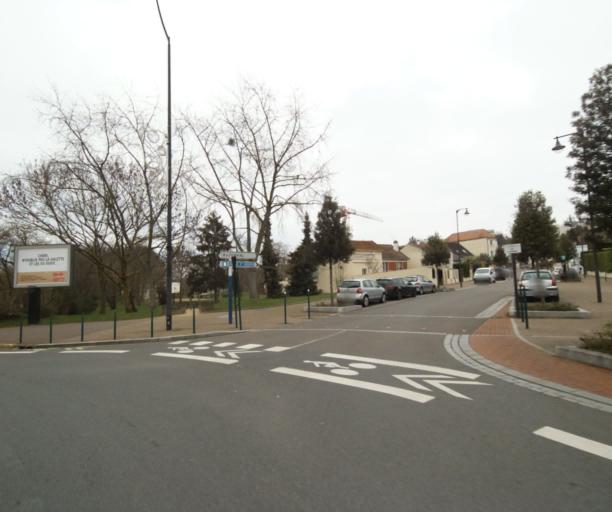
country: FR
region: Ile-de-France
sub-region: Departement des Hauts-de-Seine
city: Rueil-Malmaison
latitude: 48.8586
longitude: 2.1898
